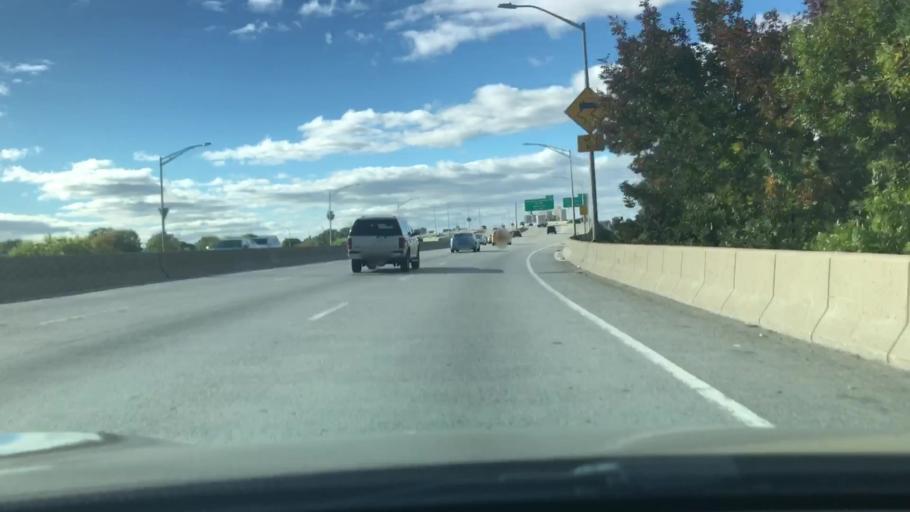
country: US
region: New York
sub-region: Queens County
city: Jamaica
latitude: 40.7470
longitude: -73.8353
